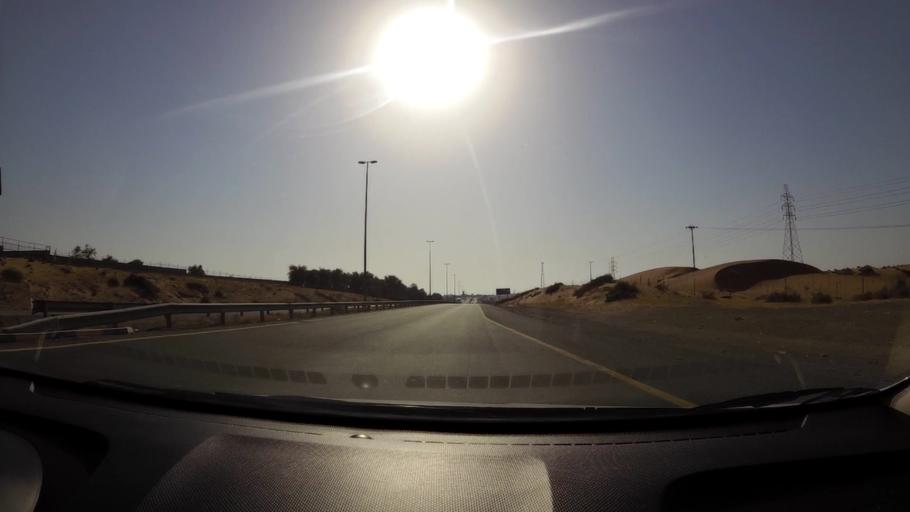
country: AE
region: Umm al Qaywayn
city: Umm al Qaywayn
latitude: 25.4416
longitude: 55.6377
